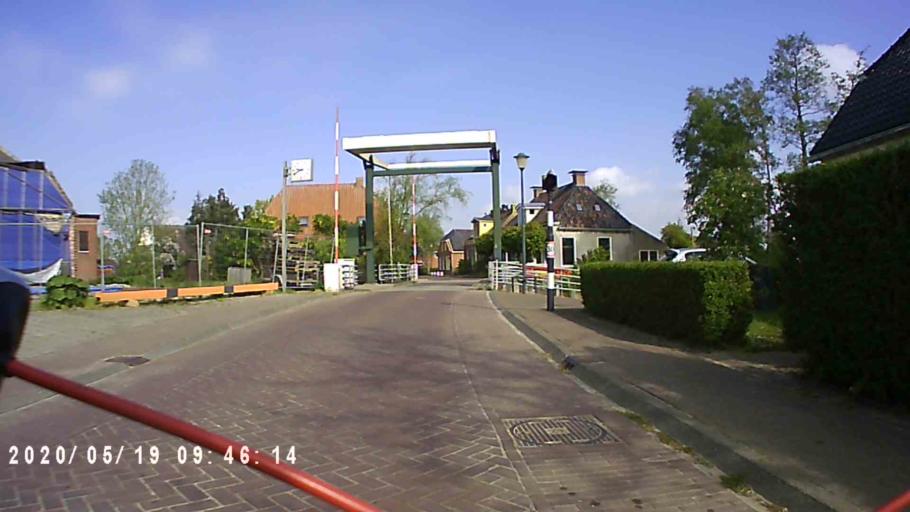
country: NL
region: Groningen
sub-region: Gemeente Zuidhorn
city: Grijpskerk
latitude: 53.2813
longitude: 6.2684
